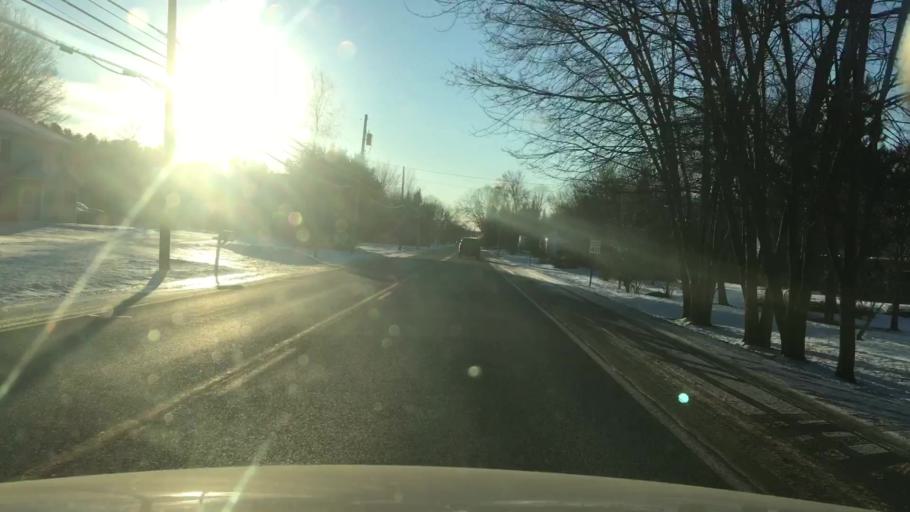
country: US
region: Maine
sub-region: Penobscot County
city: Veazie
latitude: 44.8191
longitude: -68.7181
